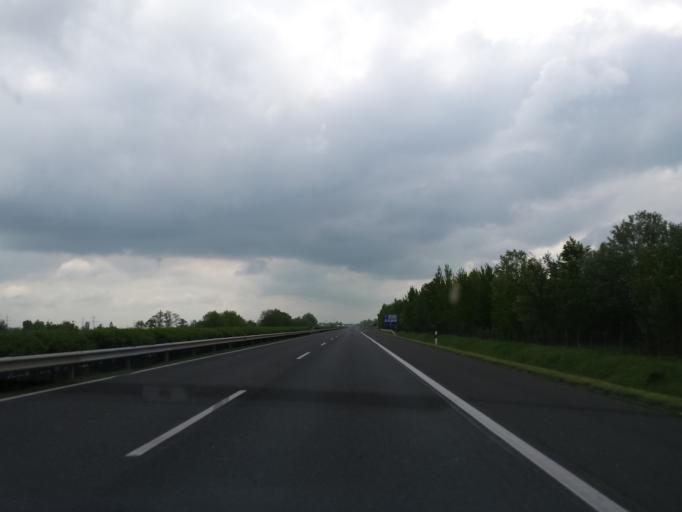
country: HU
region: Gyor-Moson-Sopron
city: Otteveny
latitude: 47.7103
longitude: 17.4819
